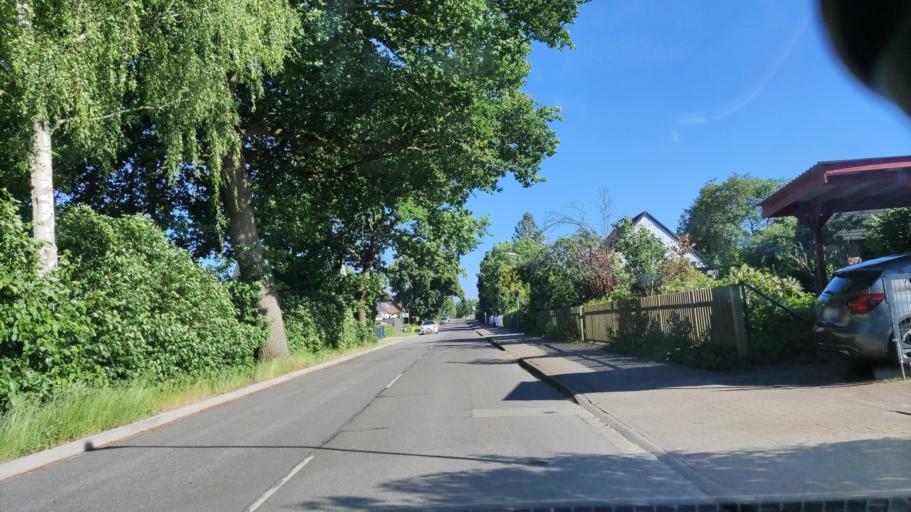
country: DE
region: Lower Saxony
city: Stelle
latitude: 53.3703
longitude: 10.1232
